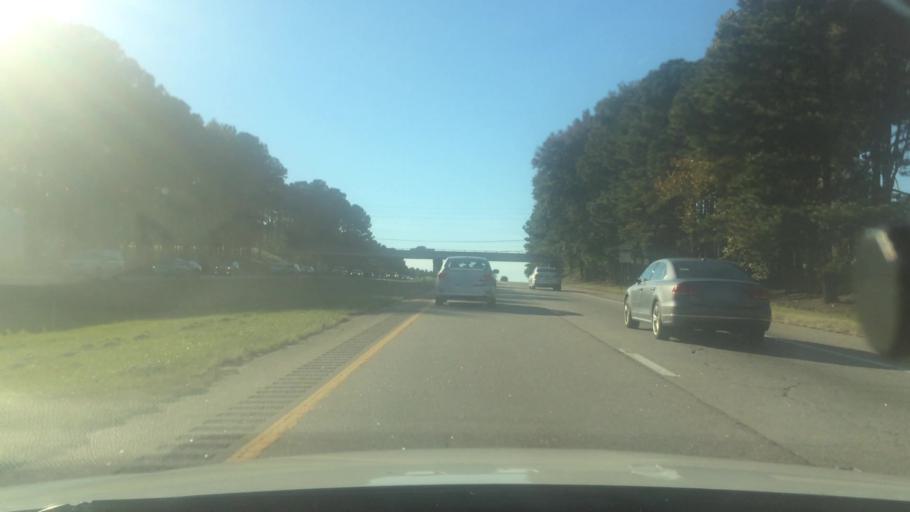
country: US
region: North Carolina
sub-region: Wake County
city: West Raleigh
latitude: 35.8040
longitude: -78.7048
